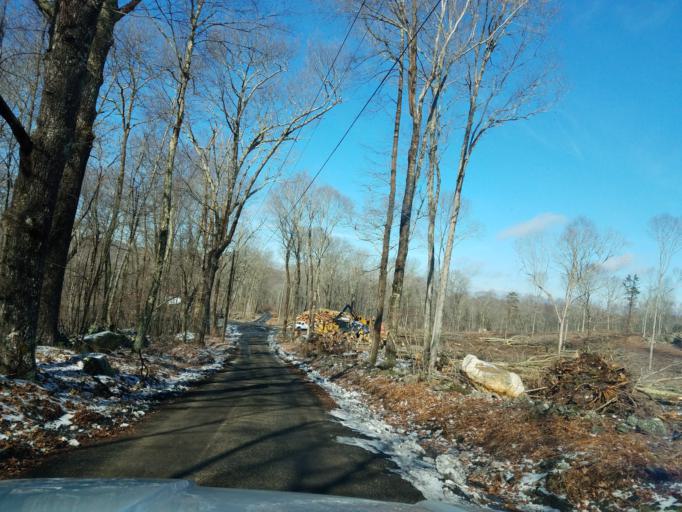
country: US
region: Connecticut
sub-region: New London County
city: Preston City
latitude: 41.4857
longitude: -71.9286
